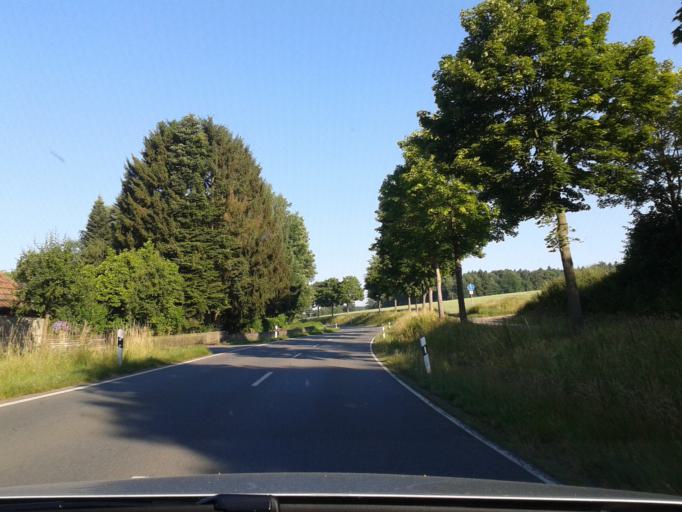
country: DE
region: North Rhine-Westphalia
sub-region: Regierungsbezirk Detmold
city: Dorentrup
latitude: 52.0300
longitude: 9.0241
